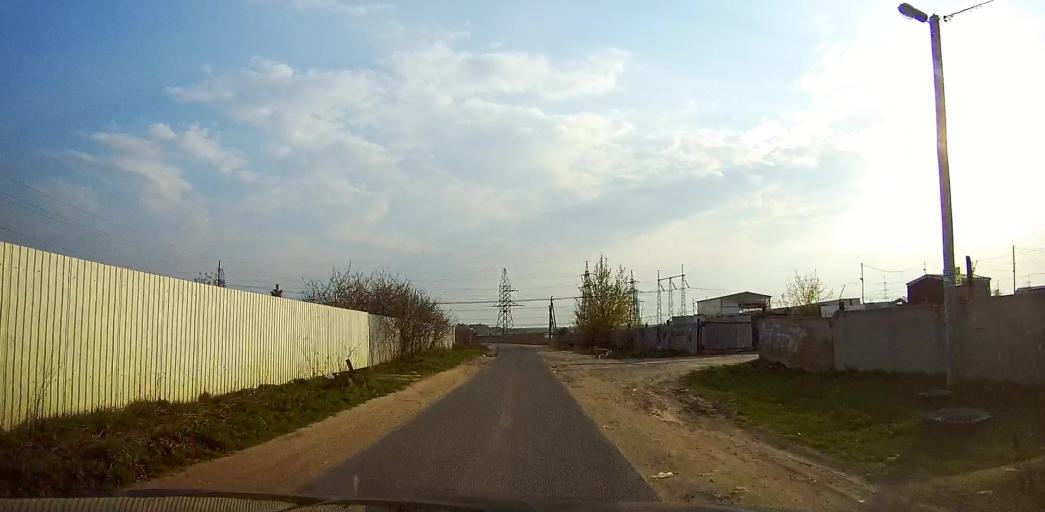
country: RU
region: Moskovskaya
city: Andreyevskoye
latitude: 55.5394
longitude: 37.9708
